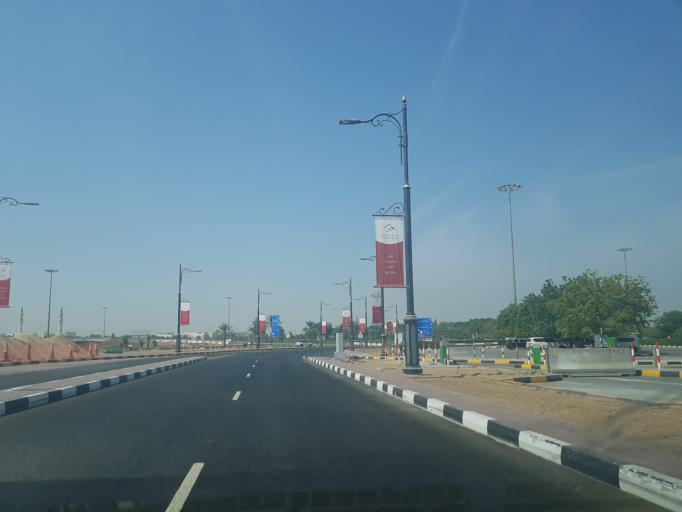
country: AE
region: Ash Shariqah
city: Sharjah
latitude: 25.3193
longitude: 55.5210
